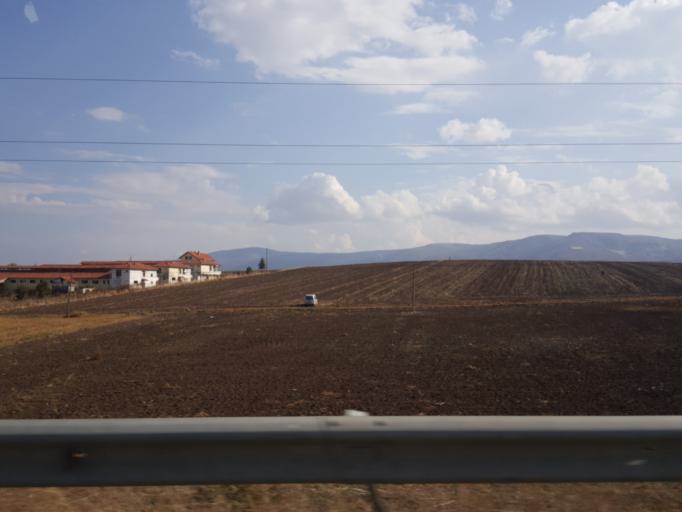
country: TR
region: Corum
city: Seydim
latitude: 40.4448
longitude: 34.8237
